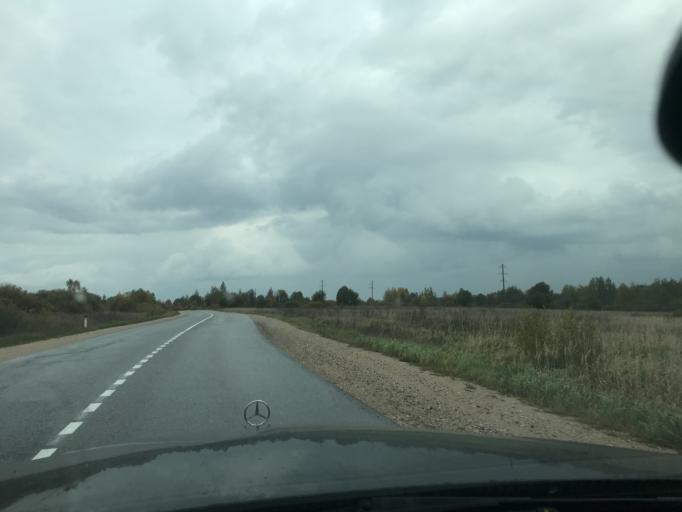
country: RU
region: Pskov
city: Izborsk
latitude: 57.6421
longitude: 27.9013
